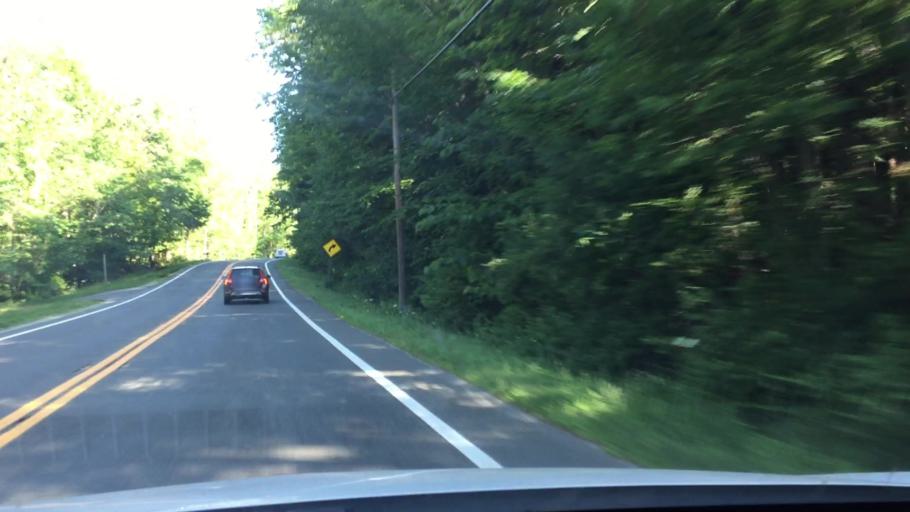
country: US
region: Massachusetts
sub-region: Berkshire County
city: Lee
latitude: 42.3276
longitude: -73.2627
